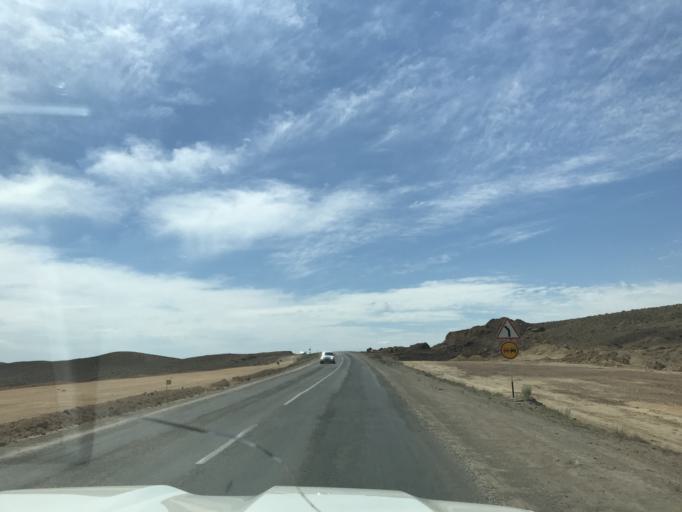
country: KZ
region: Almaty Oblysy
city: Ulken
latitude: 45.0836
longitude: 73.9701
